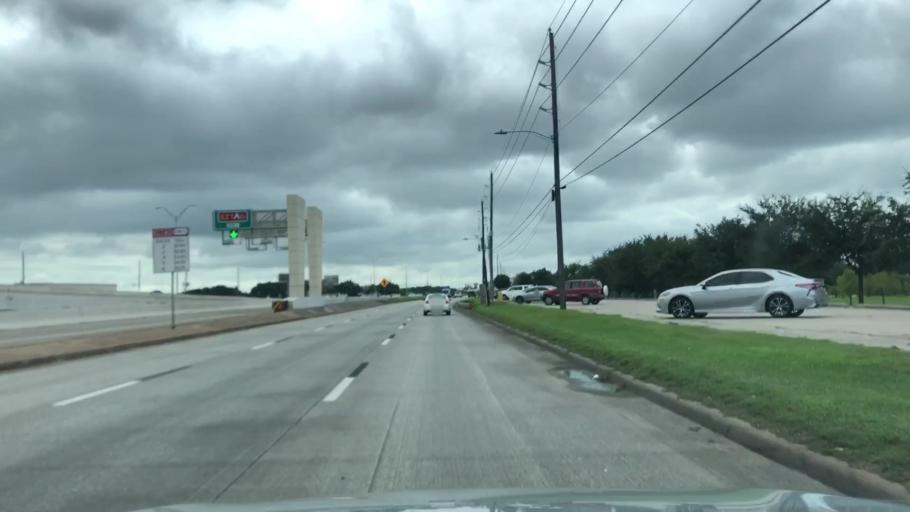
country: US
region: Texas
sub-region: Fort Bend County
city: Meadows Place
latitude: 29.7017
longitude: -95.5577
